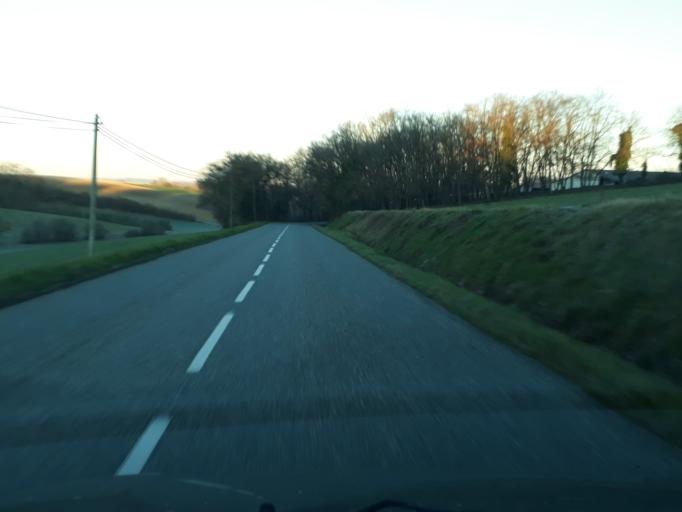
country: FR
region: Midi-Pyrenees
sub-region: Departement du Gers
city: Pavie
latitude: 43.6136
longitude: 0.6797
